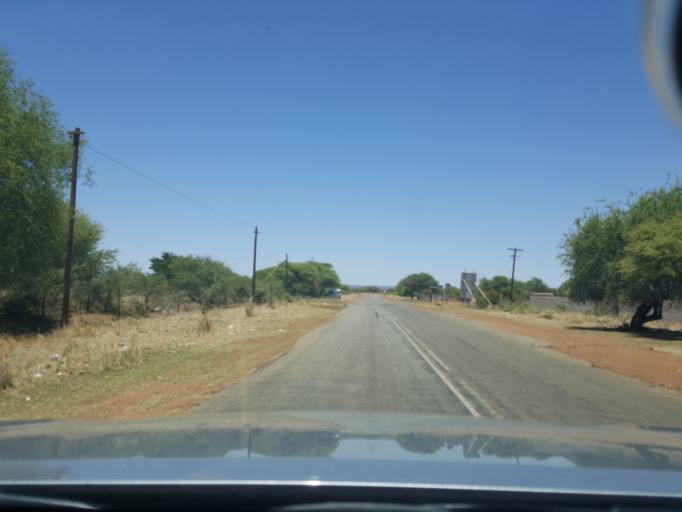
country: BW
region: South East
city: Otse
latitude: -25.1149
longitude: 25.9490
